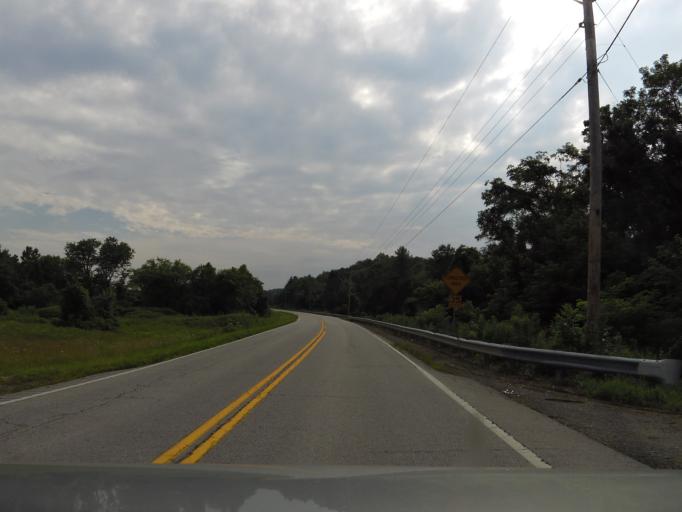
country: US
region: Kentucky
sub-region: Robertson County
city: Mount Olivet
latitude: 38.5203
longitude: -84.1846
